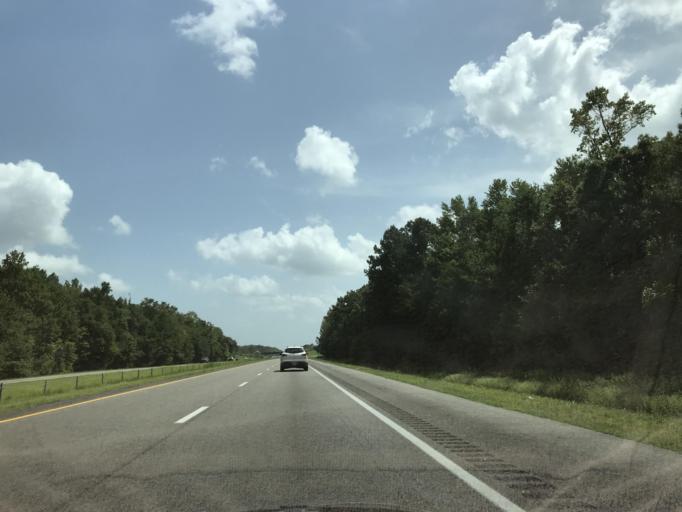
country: US
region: North Carolina
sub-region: Pender County
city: Rocky Point
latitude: 34.4484
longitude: -77.8766
